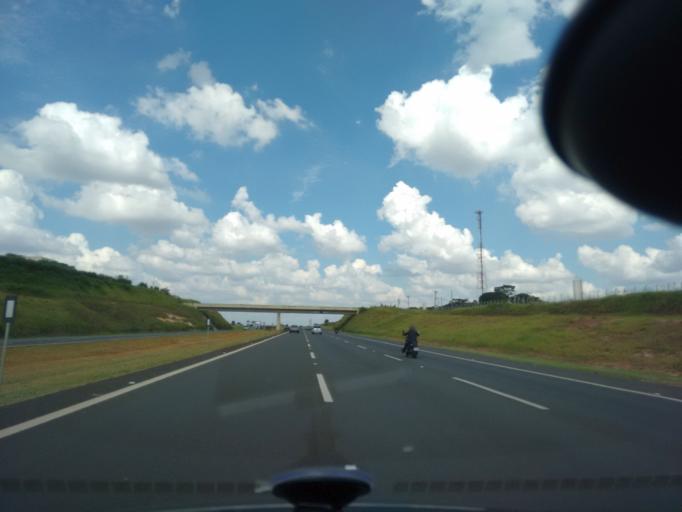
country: BR
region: Sao Paulo
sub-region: Hortolandia
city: Hortolandia
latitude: -22.9085
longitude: -47.1973
